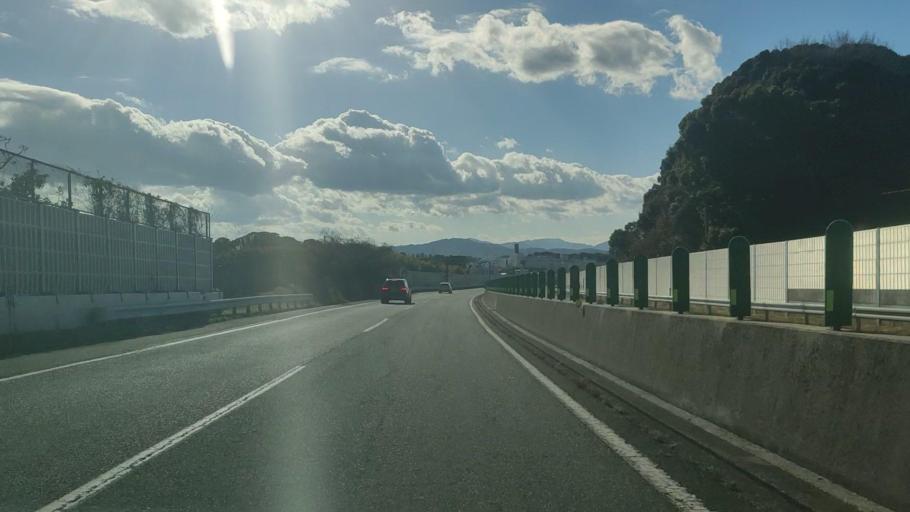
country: JP
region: Fukuoka
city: Nakama
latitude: 33.8232
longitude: 130.7613
